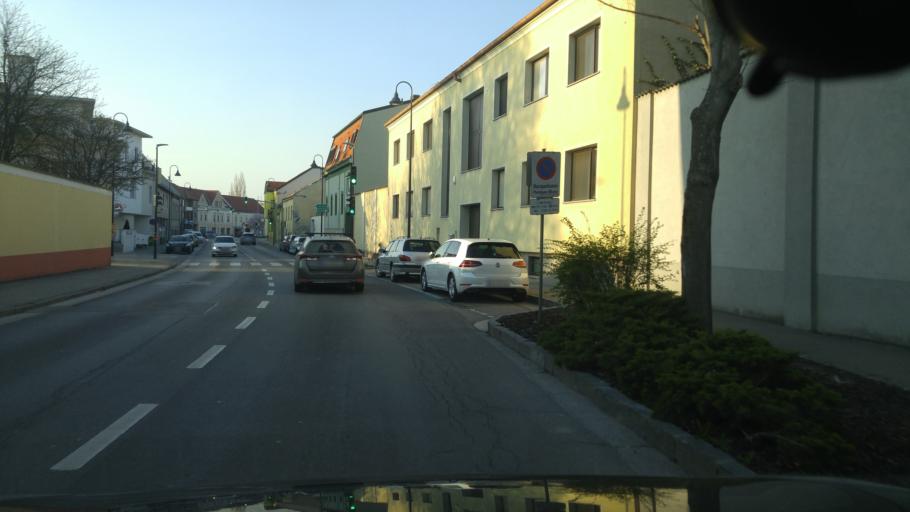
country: AT
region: Lower Austria
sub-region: Politischer Bezirk Wien-Umgebung
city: Himberg
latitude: 48.0809
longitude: 16.4402
